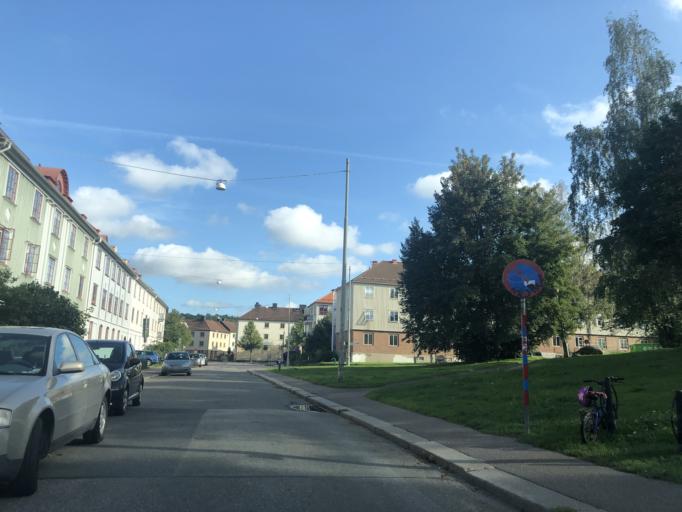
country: SE
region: Vaestra Goetaland
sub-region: Goteborg
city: Majorna
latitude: 57.6854
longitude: 11.9155
